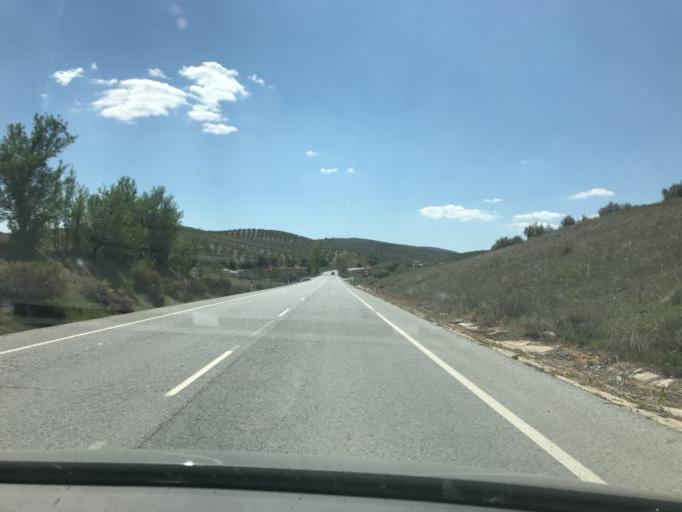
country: ES
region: Andalusia
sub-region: Provincia de Granada
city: Benalua de las Villas
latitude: 37.4333
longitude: -3.6854
